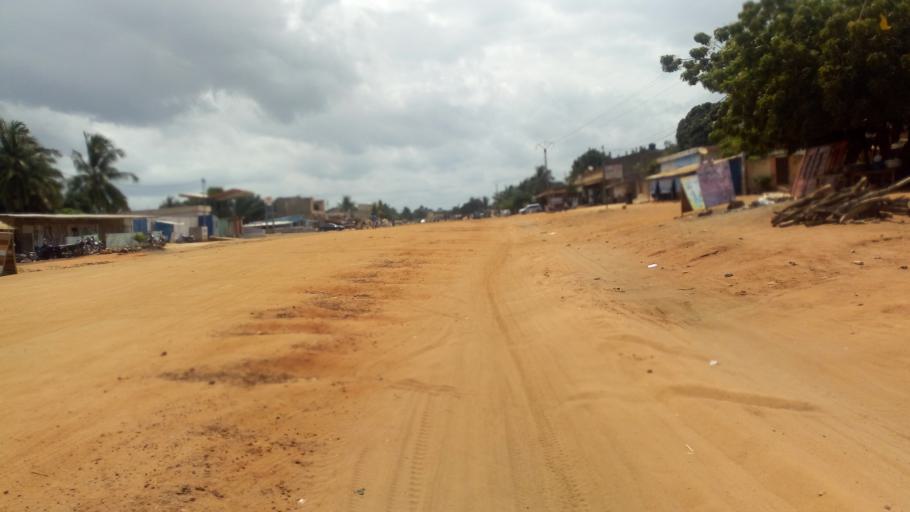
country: TG
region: Maritime
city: Lome
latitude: 6.2165
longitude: 1.1844
